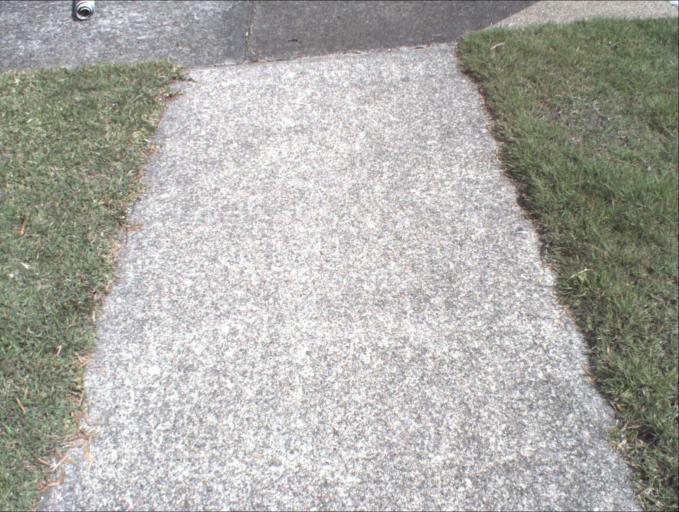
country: AU
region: Queensland
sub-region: Logan
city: Woodridge
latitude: -27.6616
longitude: 153.0590
